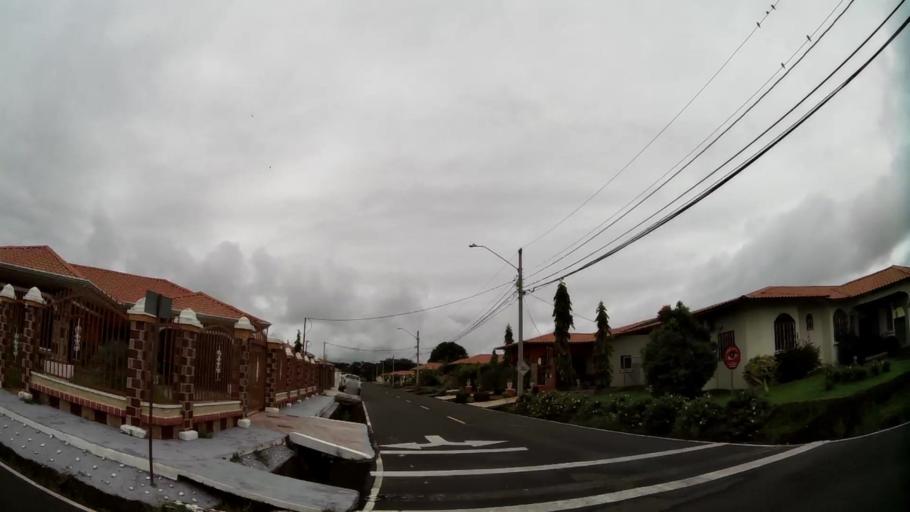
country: PA
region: Chiriqui
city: David
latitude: 8.4357
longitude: -82.4431
